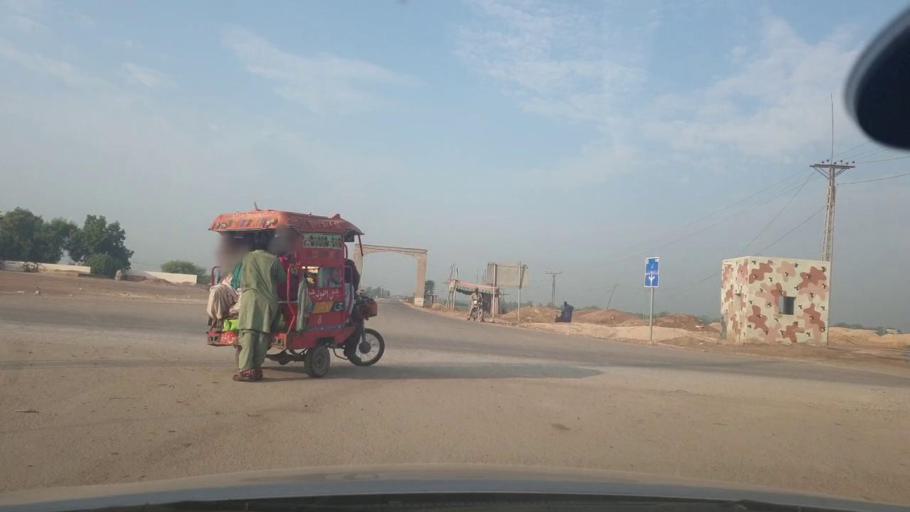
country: PK
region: Sindh
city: Jacobabad
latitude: 28.2630
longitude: 68.4169
